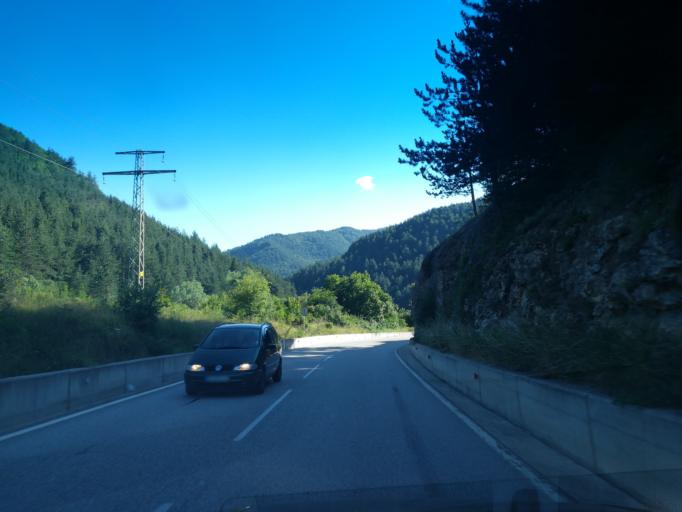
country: BG
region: Smolyan
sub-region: Obshtina Chepelare
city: Chepelare
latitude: 41.8506
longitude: 24.6836
